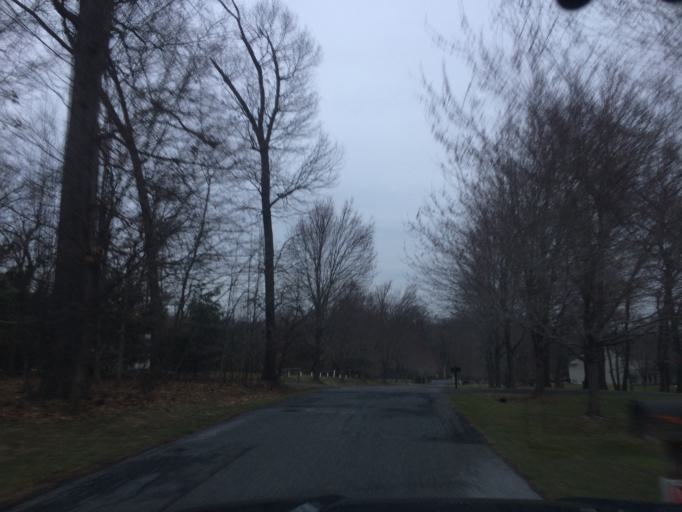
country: US
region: Maryland
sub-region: Carroll County
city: Sykesville
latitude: 39.2895
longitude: -76.9976
